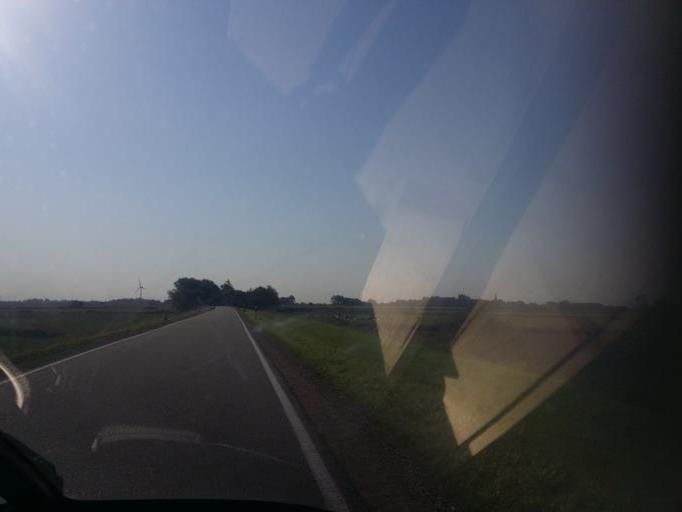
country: DE
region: Schleswig-Holstein
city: Emmelsbull-Horsbull
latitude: 54.7887
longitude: 8.7292
